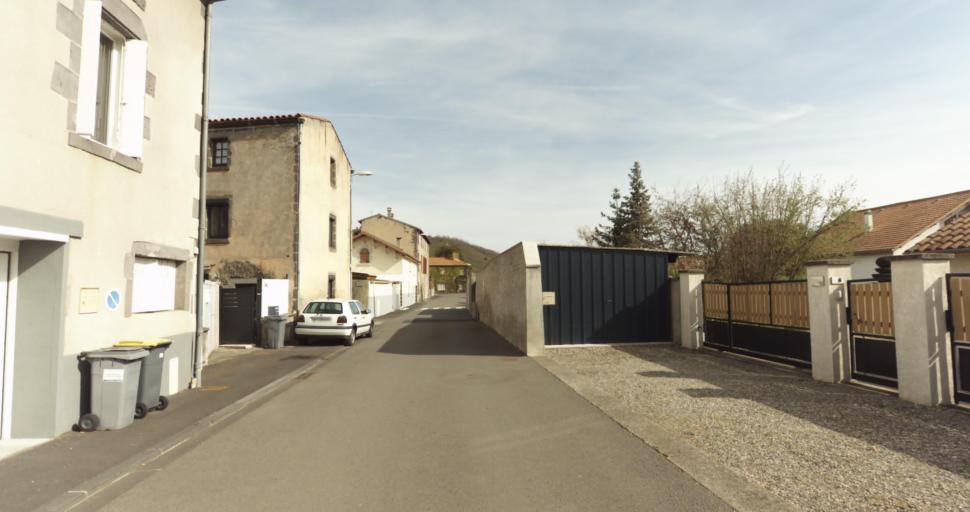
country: FR
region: Auvergne
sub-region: Departement du Puy-de-Dome
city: Blanzat
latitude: 45.8325
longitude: 3.0855
